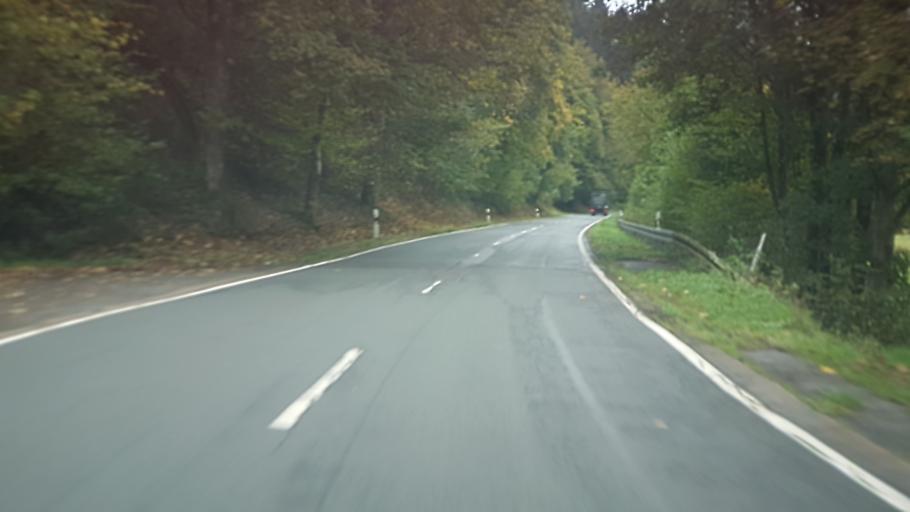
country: DE
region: North Rhine-Westphalia
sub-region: Regierungsbezirk Arnsberg
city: Herscheid
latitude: 51.2000
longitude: 7.6952
